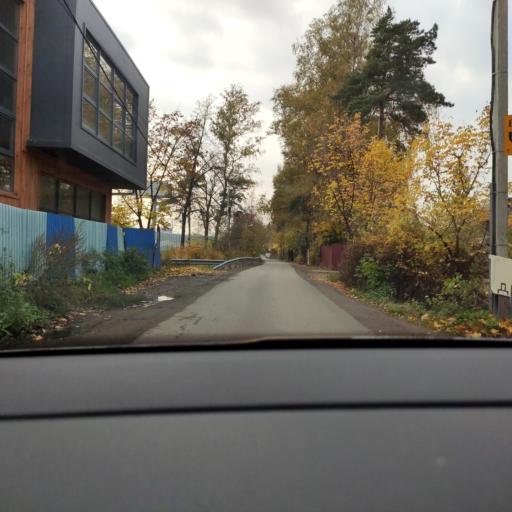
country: RU
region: Moskovskaya
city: Druzhba
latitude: 55.8980
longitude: 37.7508
